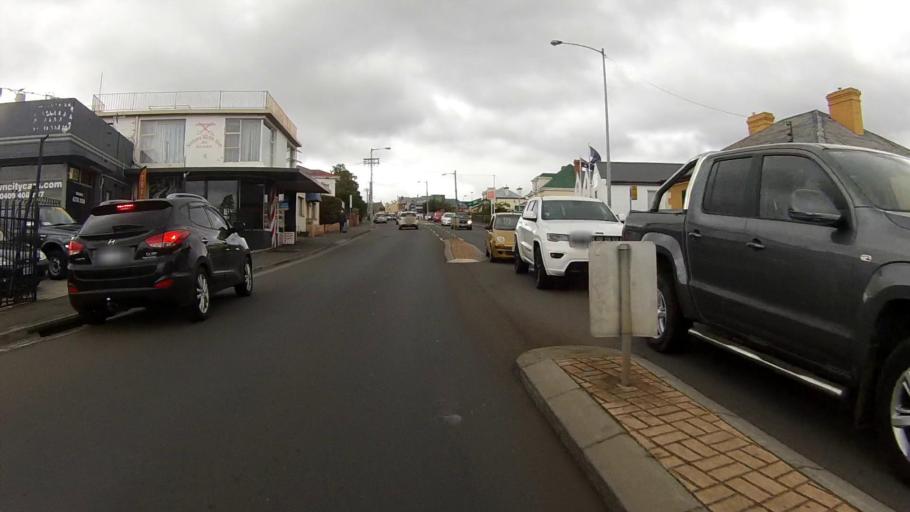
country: AU
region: Tasmania
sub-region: Hobart
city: New Town
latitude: -42.8561
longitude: 147.3037
